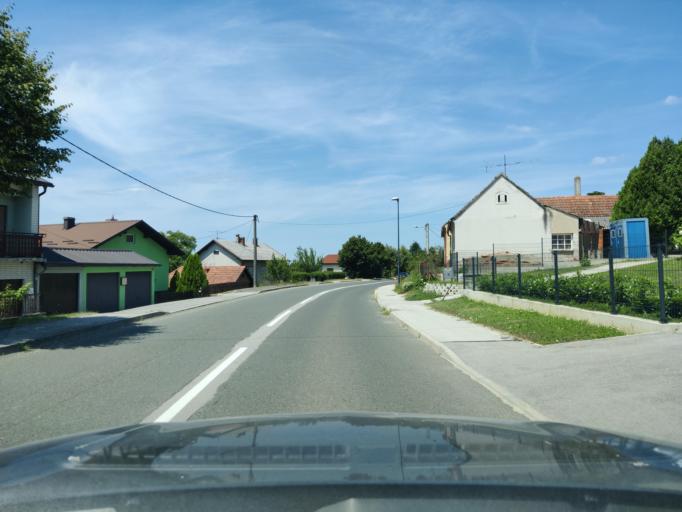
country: SI
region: Lendava-Lendva
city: Lendava
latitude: 46.5764
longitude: 16.4465
